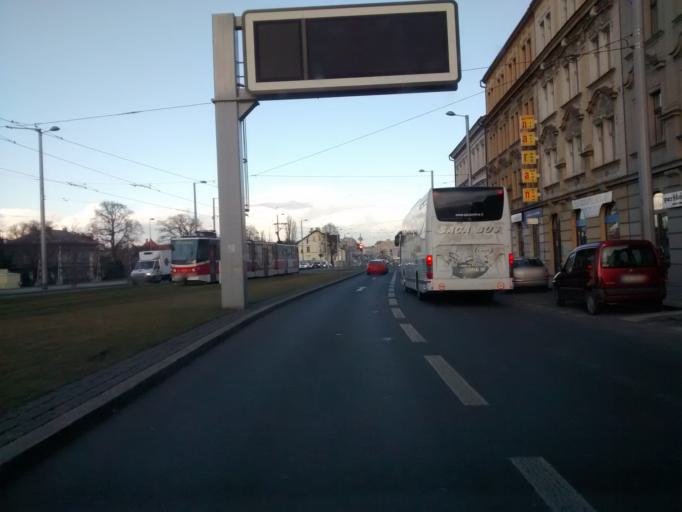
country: CZ
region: Praha
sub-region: Praha 1
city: Mala Strana
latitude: 50.0974
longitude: 14.4060
